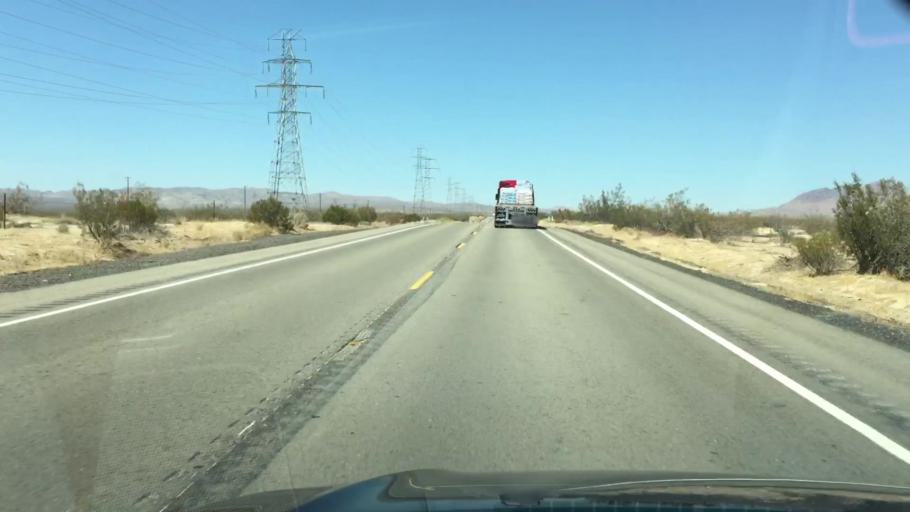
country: US
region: California
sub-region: Kern County
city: Boron
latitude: 35.2234
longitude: -117.6060
